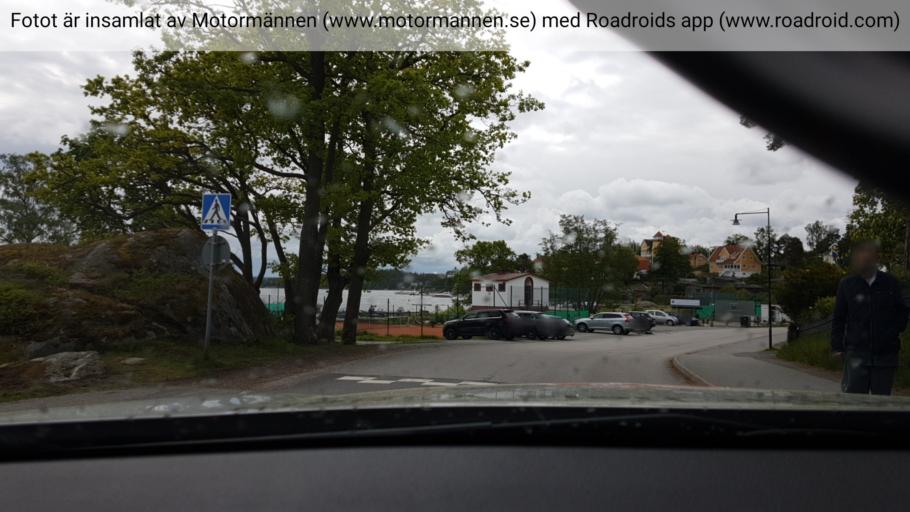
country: SE
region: Stockholm
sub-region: Nacka Kommun
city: Saltsjobaden
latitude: 59.2707
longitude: 18.3087
